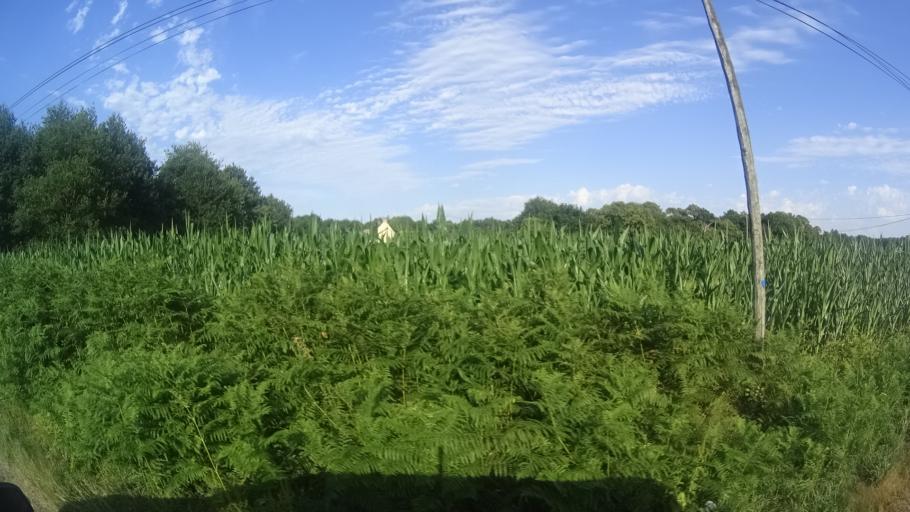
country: FR
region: Brittany
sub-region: Departement du Morbihan
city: Saint-Jean-la-Poterie
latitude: 47.6489
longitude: -2.1299
